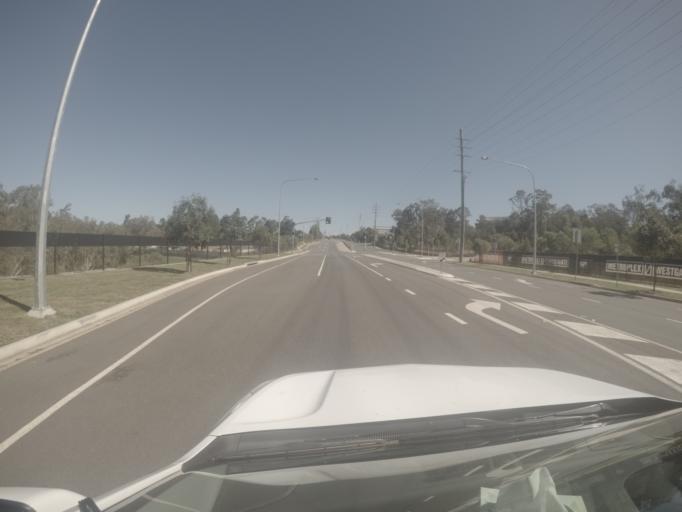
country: AU
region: Queensland
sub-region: Brisbane
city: Wacol
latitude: -27.5875
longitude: 152.9368
